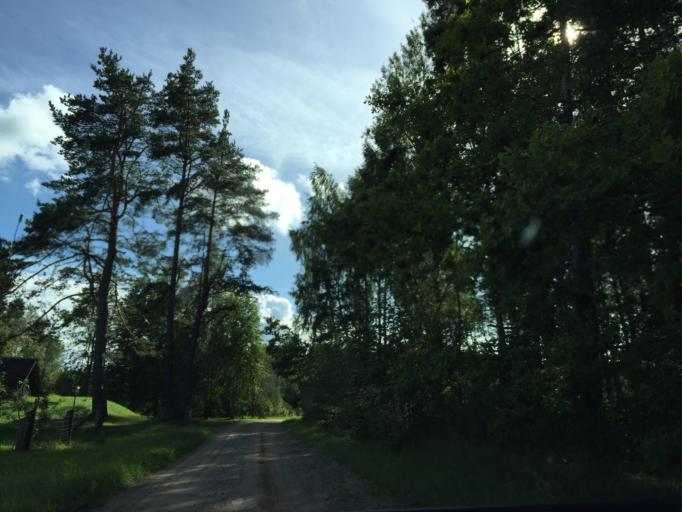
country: LV
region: Kuldigas Rajons
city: Kuldiga
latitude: 56.9873
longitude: 21.8020
